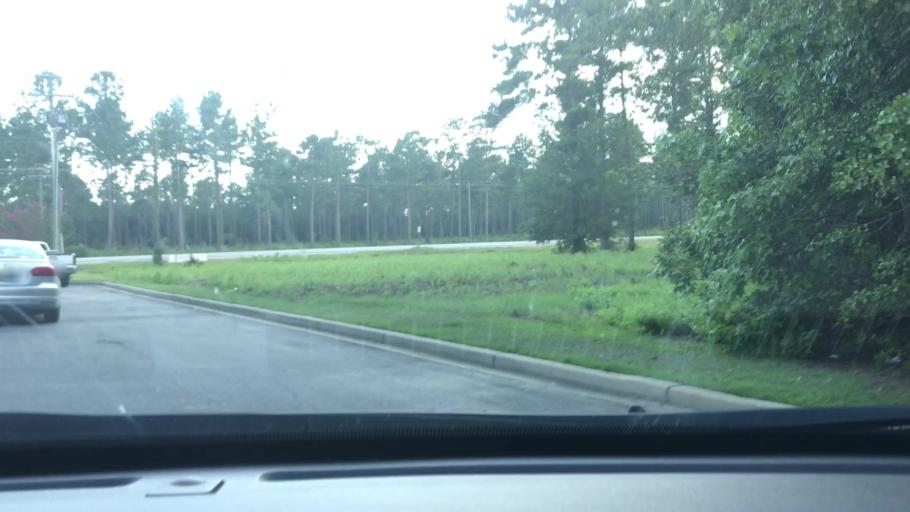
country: US
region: South Carolina
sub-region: Sumter County
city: East Sumter
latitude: 33.9036
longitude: -80.0965
